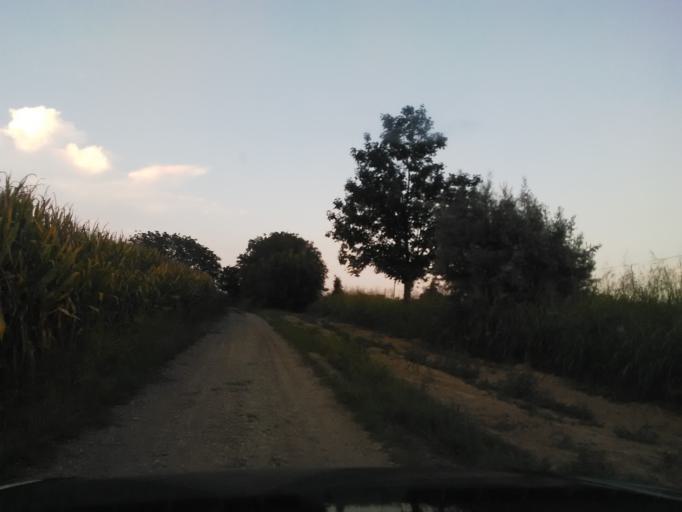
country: IT
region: Piedmont
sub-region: Provincia di Vercelli
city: Cigliano
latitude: 45.3090
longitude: 8.0443
